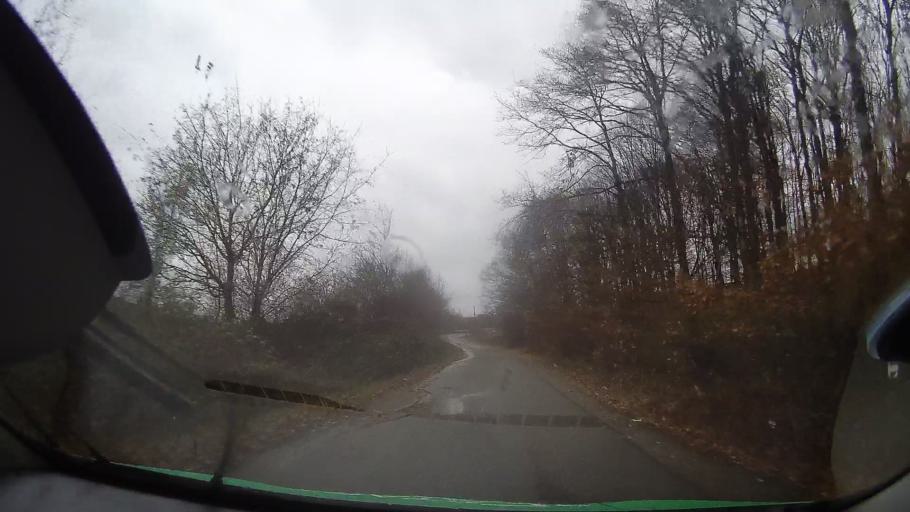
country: RO
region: Bihor
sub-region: Comuna Rabagani
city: Rabagani
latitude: 46.7260
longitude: 22.2400
